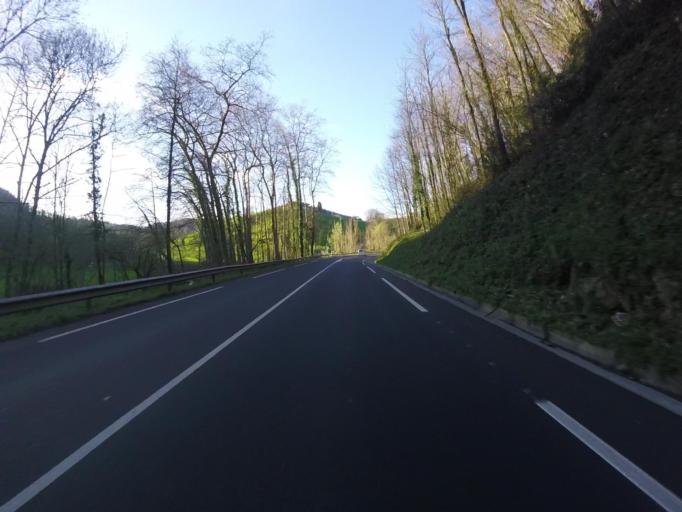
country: ES
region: Basque Country
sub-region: Provincia de Guipuzcoa
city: Errenteria
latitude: 43.2881
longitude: -1.8883
